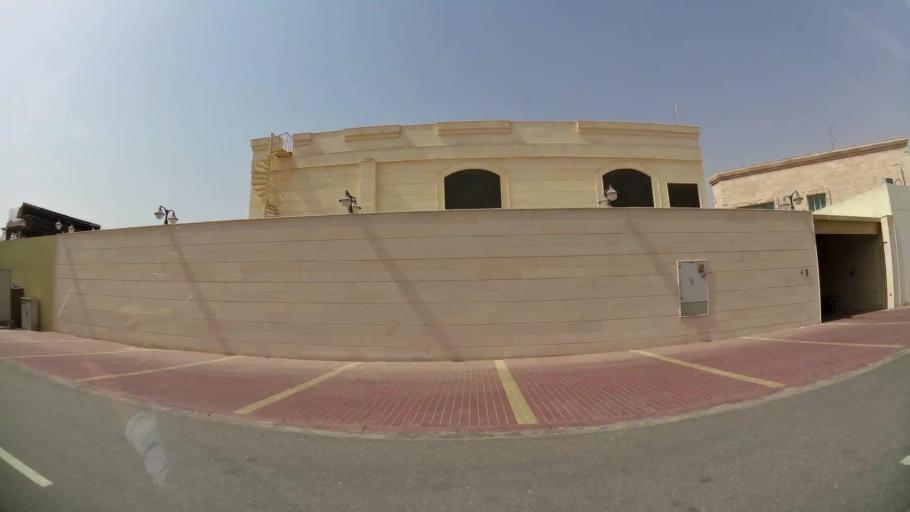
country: AE
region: Ash Shariqah
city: Sharjah
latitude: 25.2418
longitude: 55.4511
